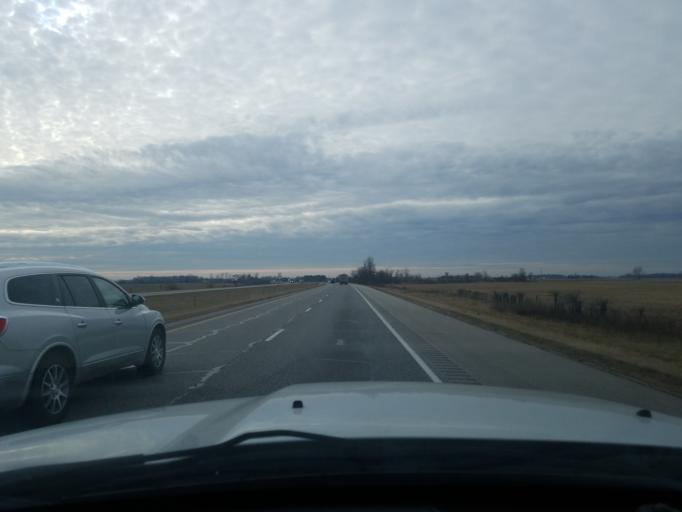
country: US
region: Indiana
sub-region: Huntington County
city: Warren
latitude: 40.6918
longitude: -85.4730
